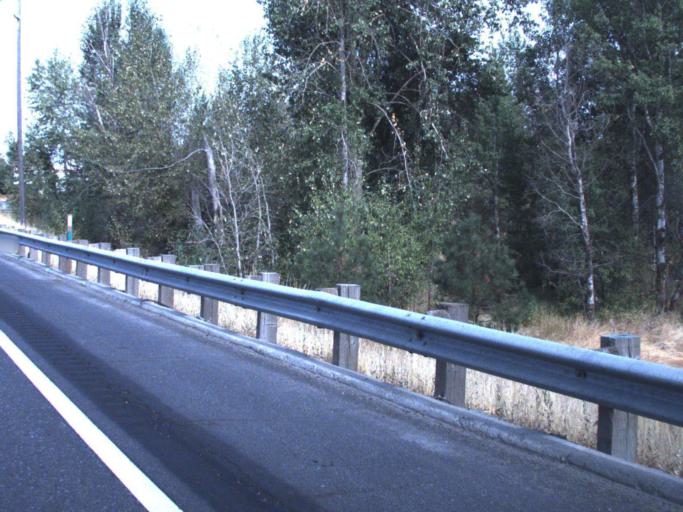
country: US
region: Washington
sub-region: Spokane County
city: Deer Park
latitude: 47.9321
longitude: -117.4672
